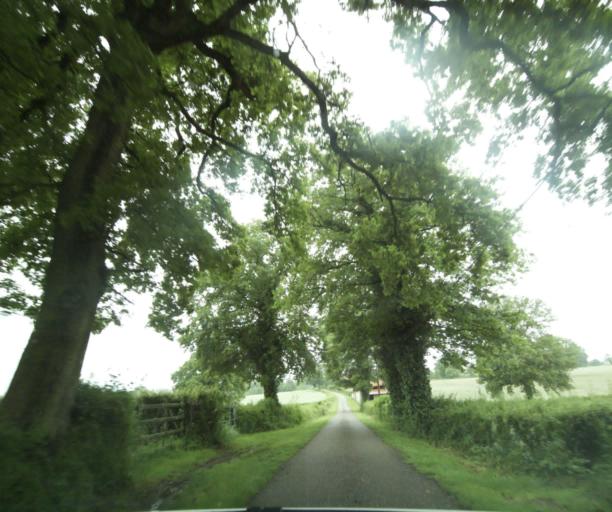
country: FR
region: Bourgogne
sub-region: Departement de Saone-et-Loire
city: Paray-le-Monial
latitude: 46.4049
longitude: 4.1869
